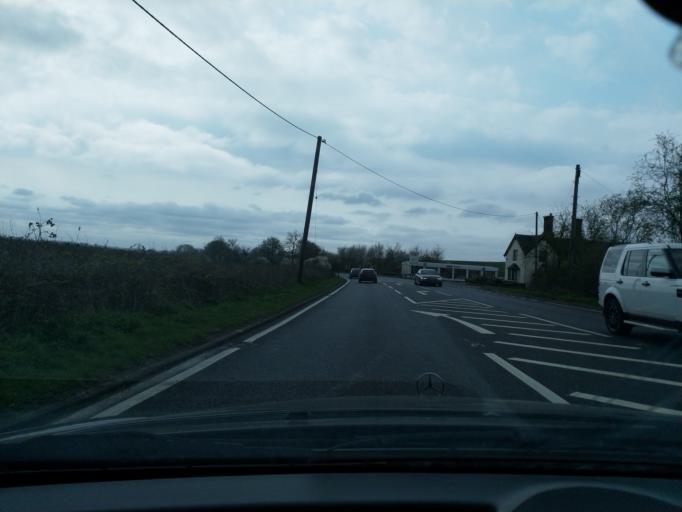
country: GB
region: England
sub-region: Warwickshire
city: Stratford-upon-Avon
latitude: 52.2247
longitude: -1.6662
